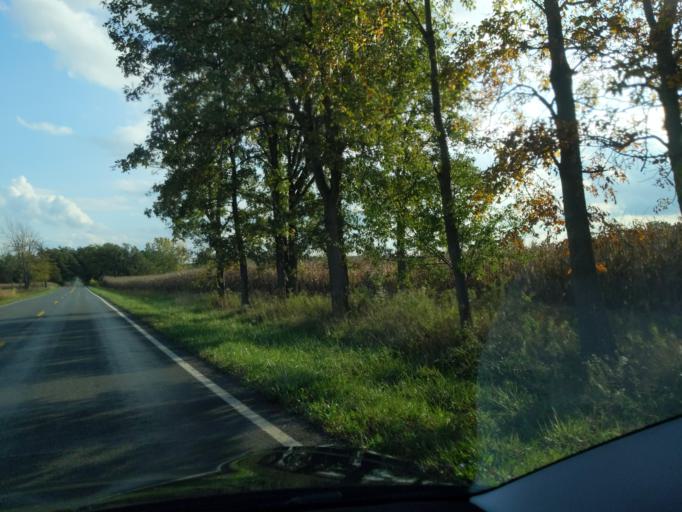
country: US
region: Michigan
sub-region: Ingham County
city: Leslie
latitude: 42.3434
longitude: -84.4629
